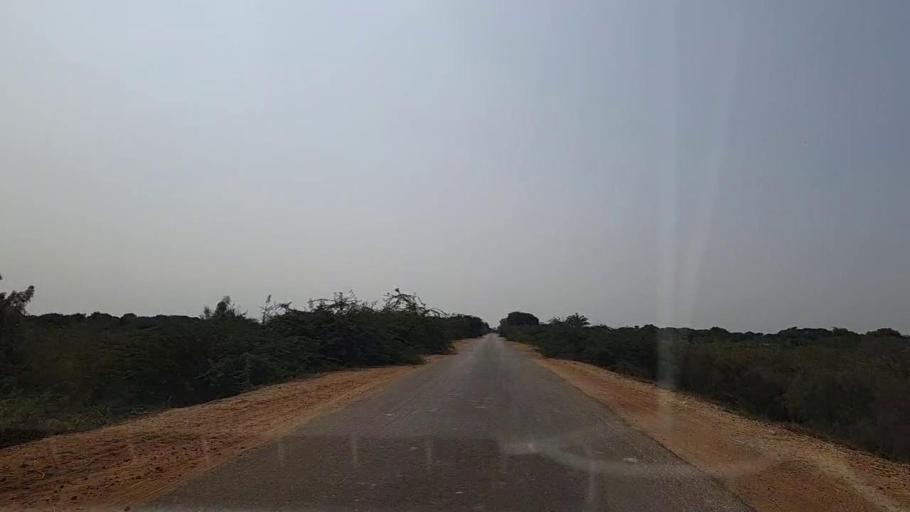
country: PK
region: Sindh
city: Chuhar Jamali
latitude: 24.2705
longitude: 67.9125
